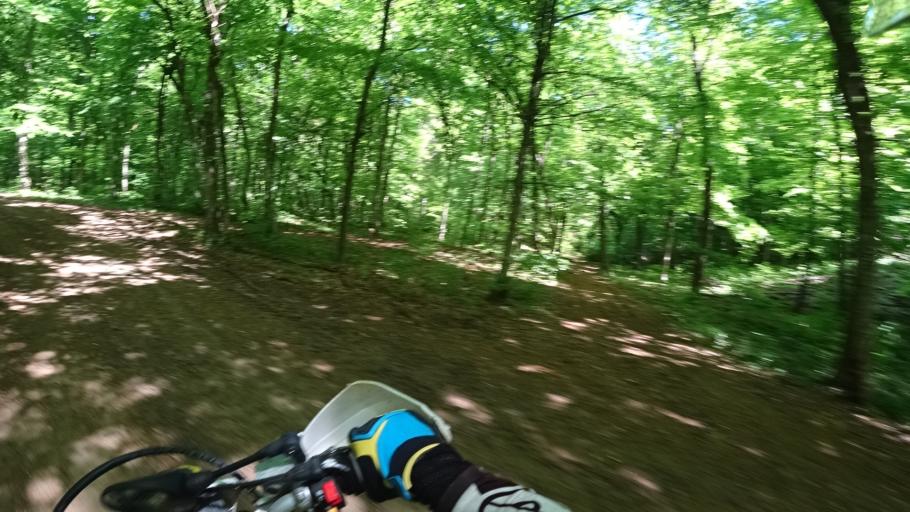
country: HR
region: Zagrebacka
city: Jablanovec
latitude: 45.8583
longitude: 15.8600
